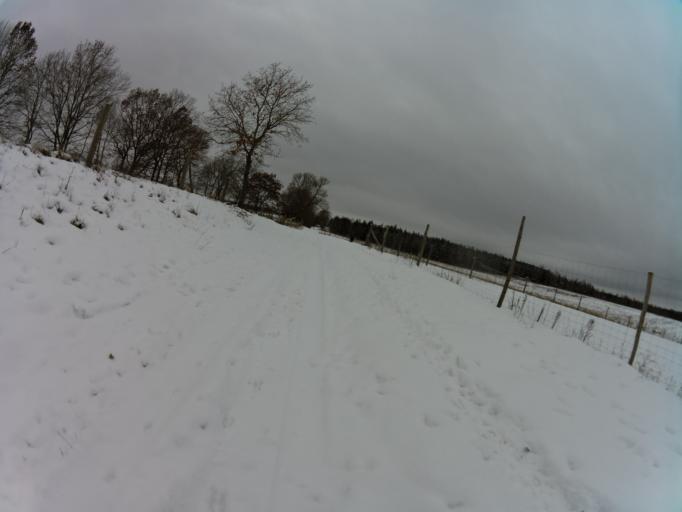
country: PL
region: West Pomeranian Voivodeship
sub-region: Powiat choszczenski
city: Recz
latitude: 53.3429
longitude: 15.5378
